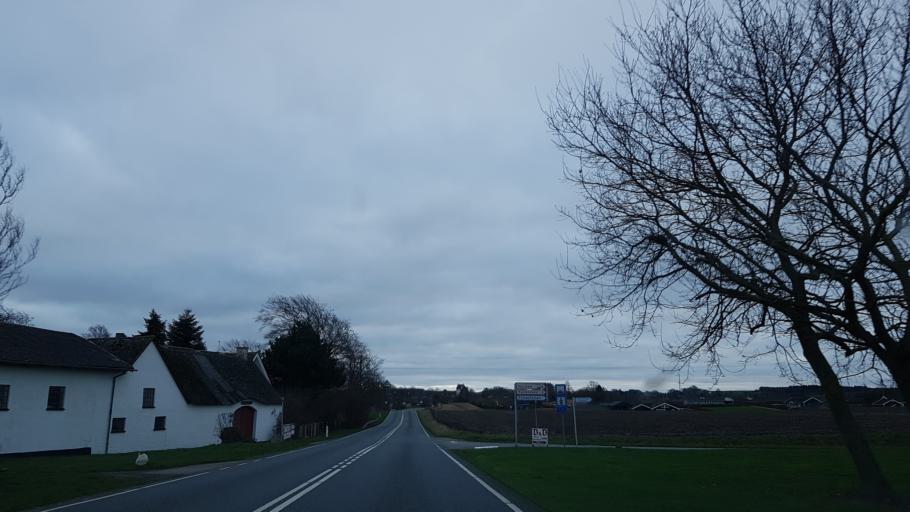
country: DK
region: Zealand
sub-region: Holbaek Kommune
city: Jyderup
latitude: 55.7231
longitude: 11.3764
